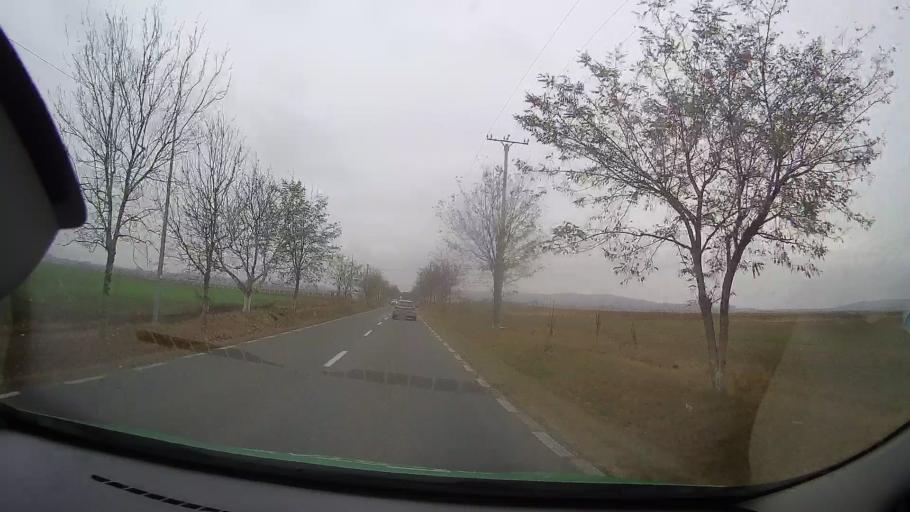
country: RO
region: Prahova
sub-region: Oras Baicoi
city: Liliesti
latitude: 45.0082
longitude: 25.8841
